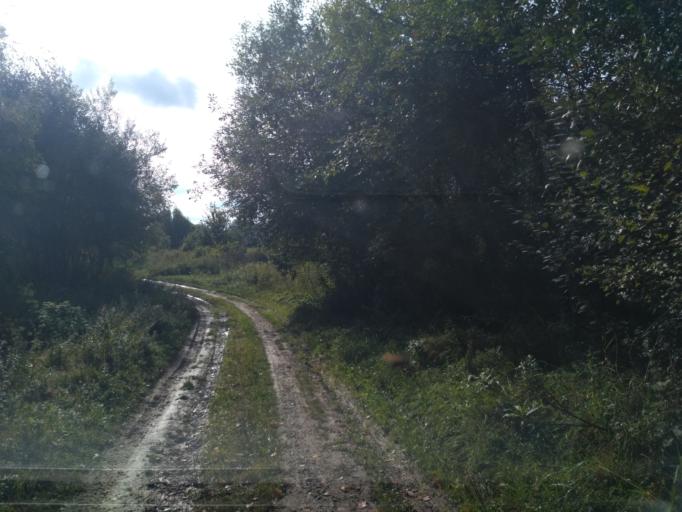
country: PL
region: Subcarpathian Voivodeship
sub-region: Powiat strzyzowski
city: Jawornik
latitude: 49.8472
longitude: 21.8580
